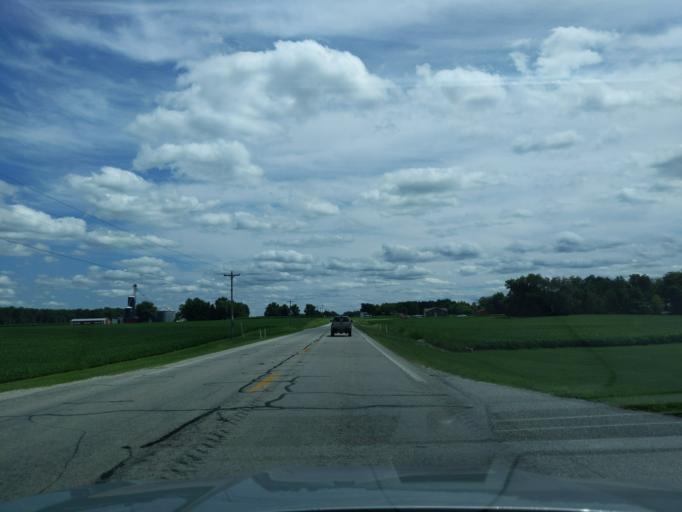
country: US
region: Indiana
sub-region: Ripley County
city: Batesville
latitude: 39.3085
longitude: -85.2775
